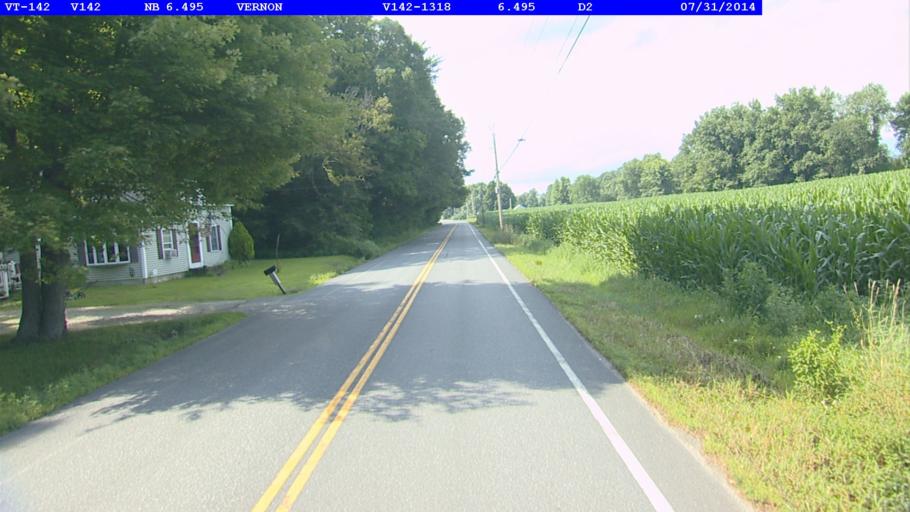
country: US
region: New Hampshire
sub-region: Cheshire County
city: Hinsdale
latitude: 42.7953
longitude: -72.5353
